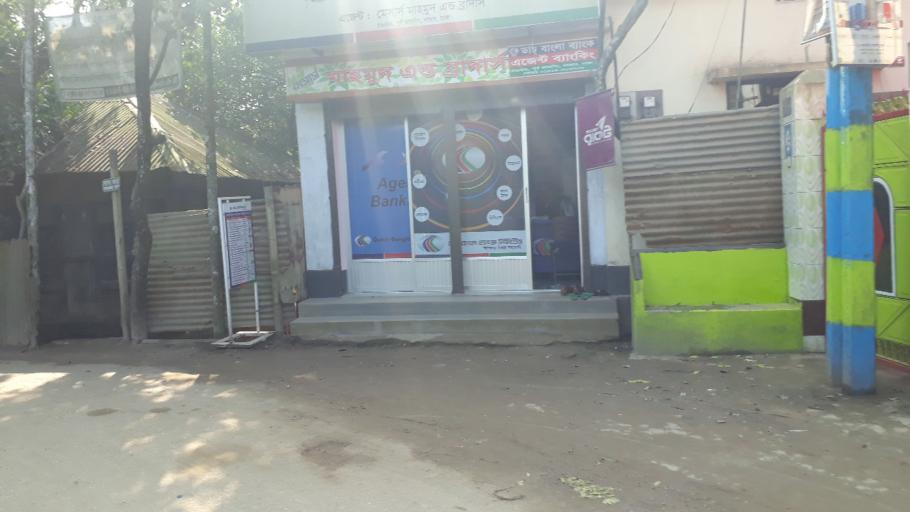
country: BD
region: Dhaka
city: Tungi
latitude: 23.8657
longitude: 90.2589
